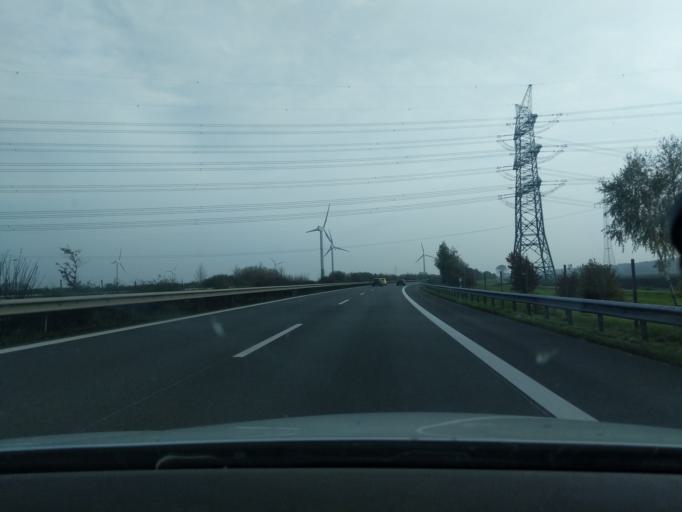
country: DE
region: Lower Saxony
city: Agathenburg
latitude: 53.5662
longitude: 9.5550
